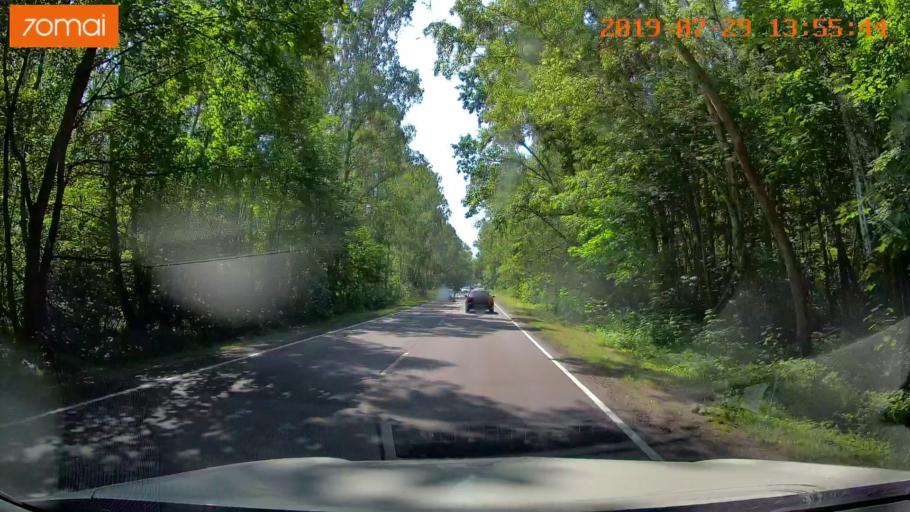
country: RU
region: Kaliningrad
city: Primorsk
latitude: 54.7129
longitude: 19.9543
